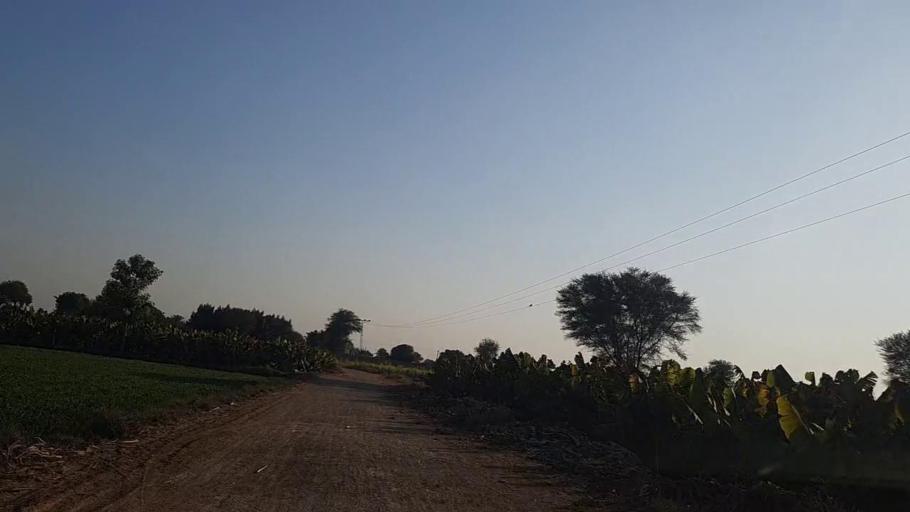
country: PK
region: Sindh
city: Sakrand
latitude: 26.3086
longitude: 68.1428
